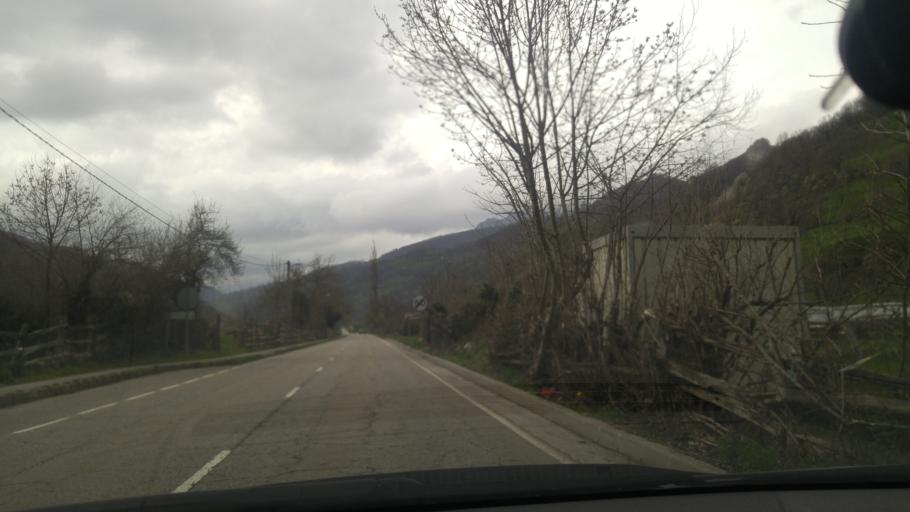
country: ES
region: Asturias
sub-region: Province of Asturias
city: Rio Aller
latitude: 43.1094
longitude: -5.5233
